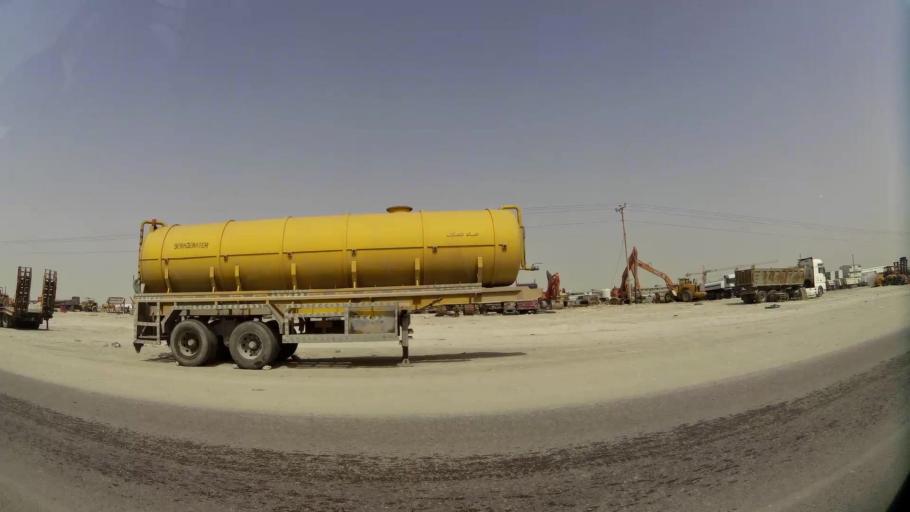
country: QA
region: Baladiyat ar Rayyan
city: Ar Rayyan
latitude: 25.2034
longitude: 51.3638
